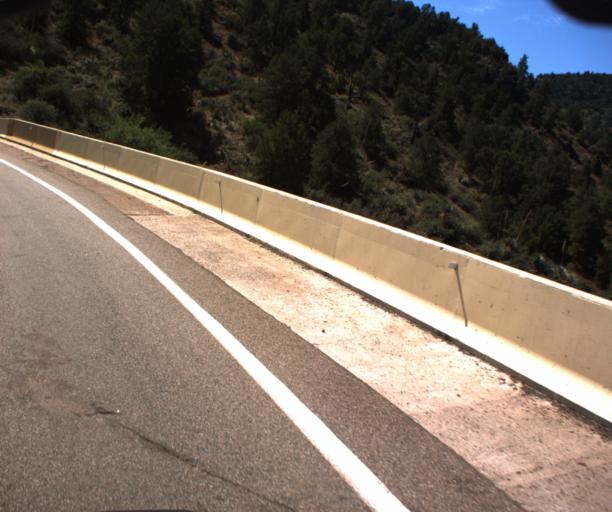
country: US
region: Arizona
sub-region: Navajo County
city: Cibecue
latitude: 33.7946
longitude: -110.5060
